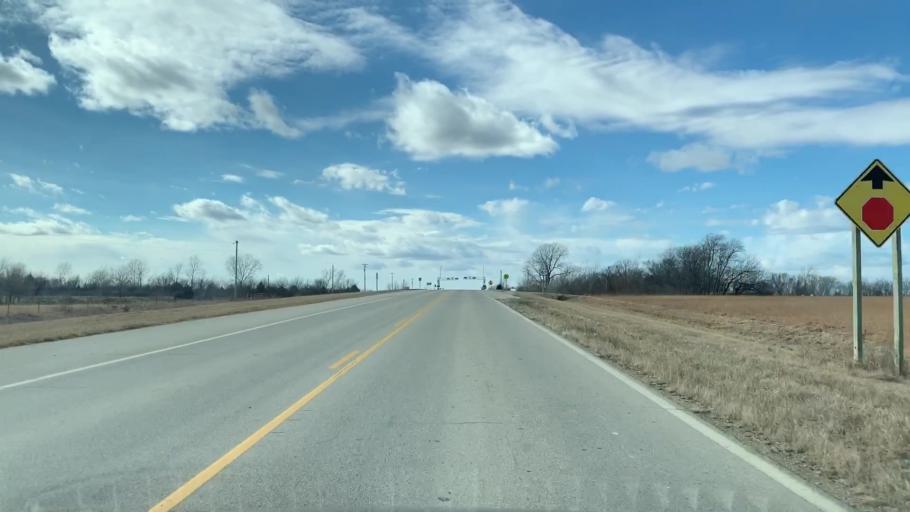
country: US
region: Kansas
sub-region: Neosho County
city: Chanute
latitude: 37.5288
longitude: -95.4667
